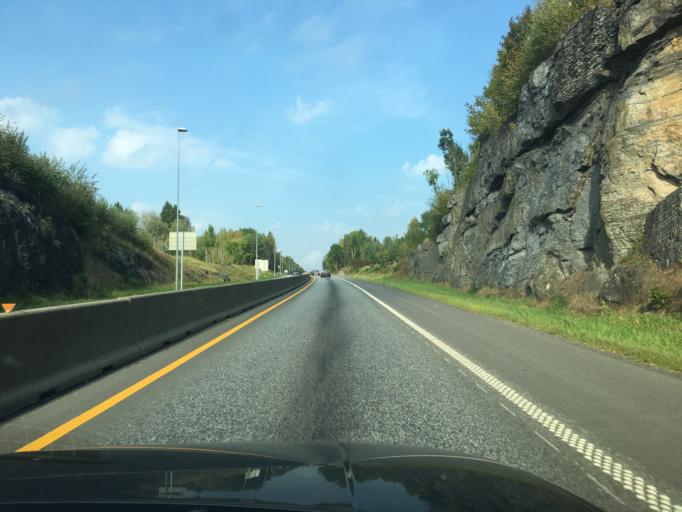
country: NO
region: Telemark
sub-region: Porsgrunn
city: Porsgrunn
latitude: 59.0823
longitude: 9.6654
